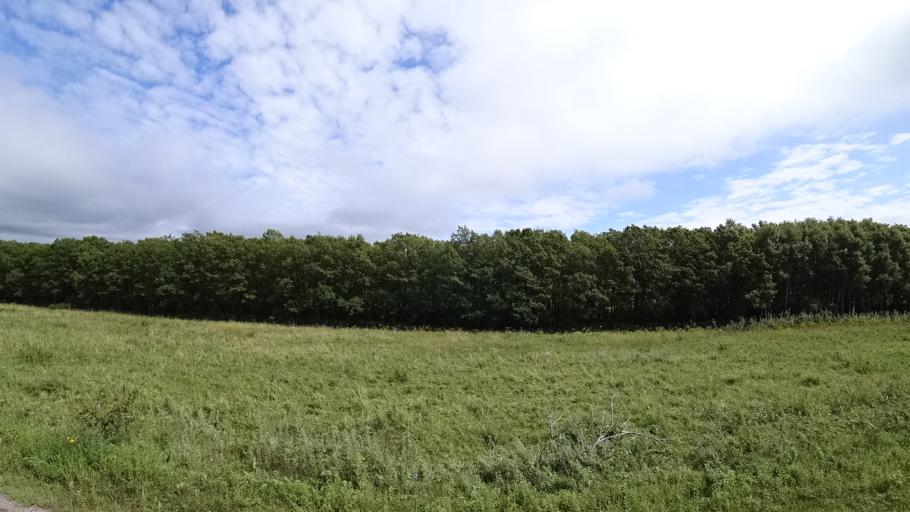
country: RU
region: Primorskiy
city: Lyalichi
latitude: 44.1451
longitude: 132.3897
